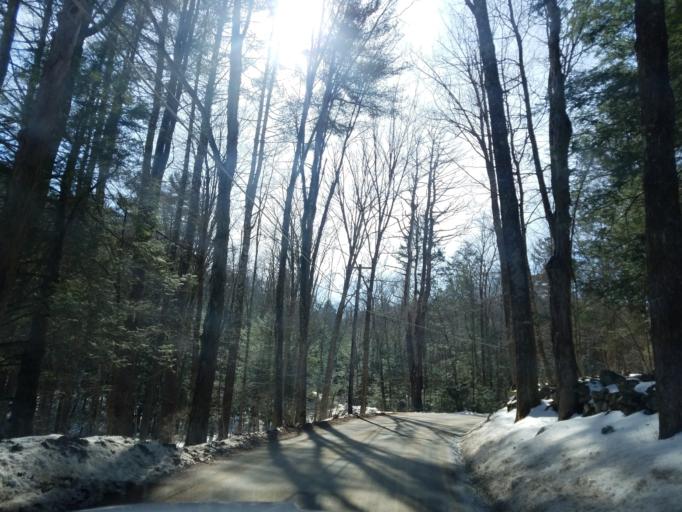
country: US
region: Connecticut
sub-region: Litchfield County
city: Canaan
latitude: 41.8746
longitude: -73.3519
